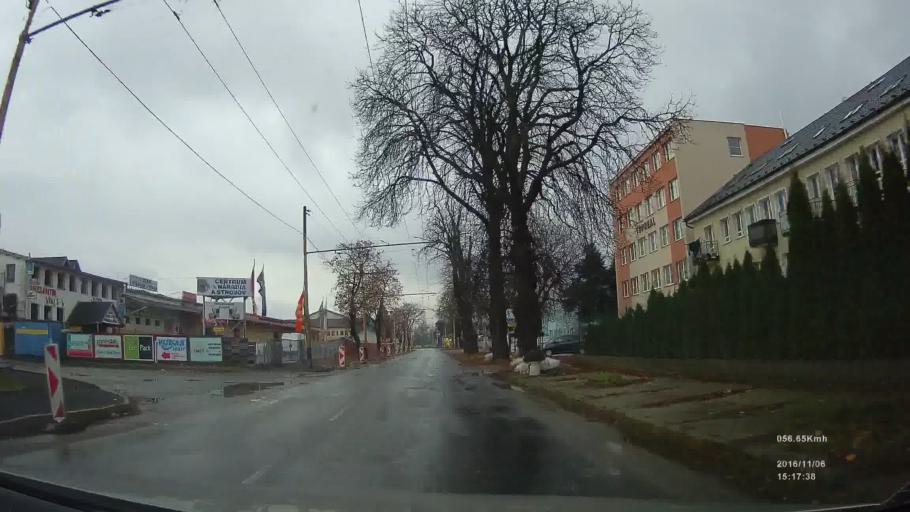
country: SK
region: Presovsky
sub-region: Okres Presov
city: Presov
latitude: 48.9782
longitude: 21.2443
